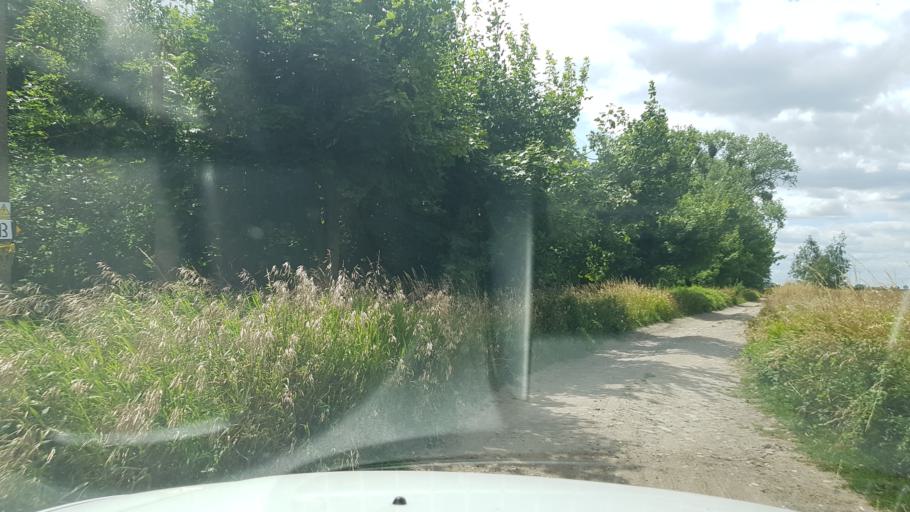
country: PL
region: West Pomeranian Voivodeship
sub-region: Powiat pyrzycki
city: Lipiany
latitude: 52.9652
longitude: 14.9911
